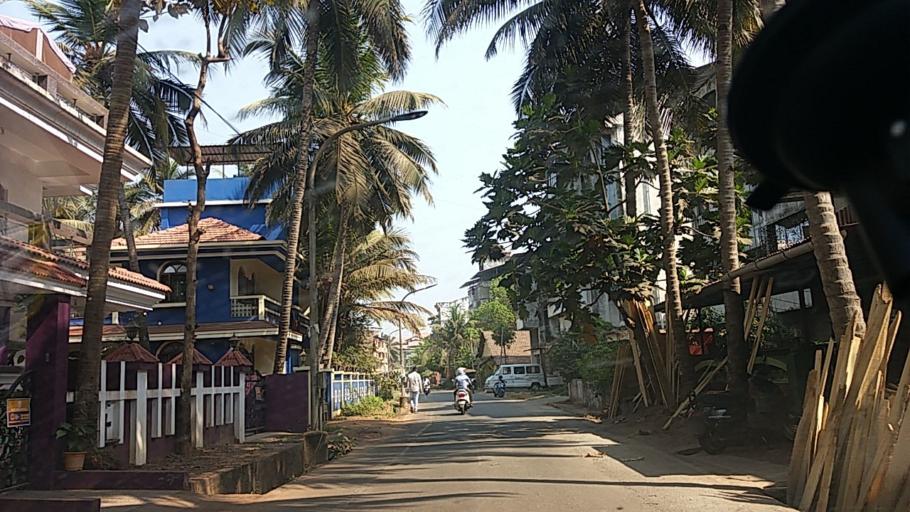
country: IN
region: Goa
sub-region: South Goa
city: Madgaon
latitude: 15.2849
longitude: 73.9537
